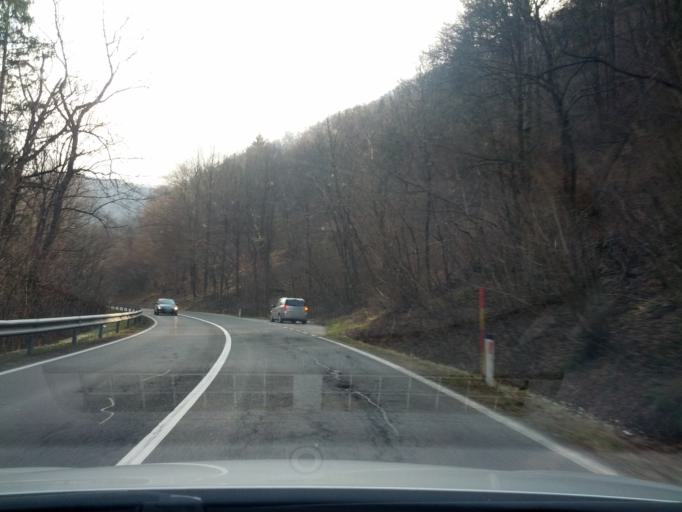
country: SI
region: Zagorje ob Savi
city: Kisovec
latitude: 46.0910
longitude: 14.9339
